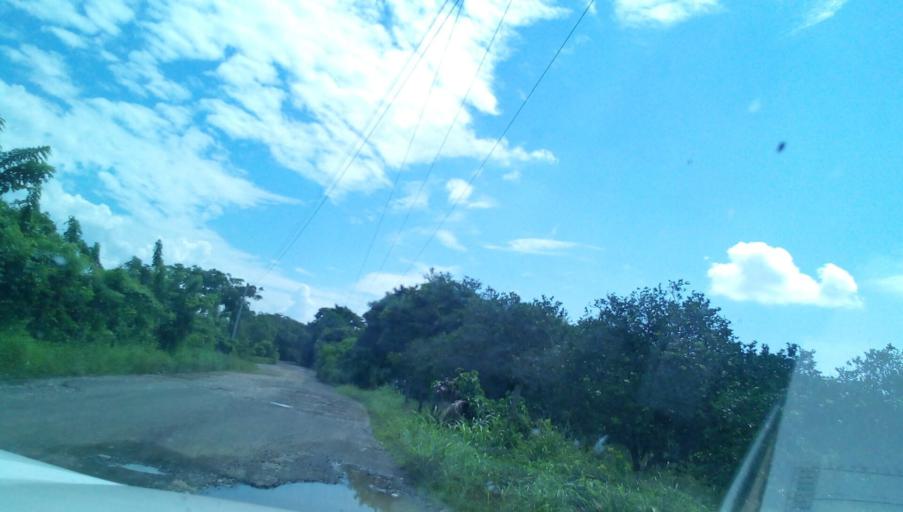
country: MX
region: Veracruz
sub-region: Alamo Temapache
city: Vegas de la Soledad y Soledad Dos
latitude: 20.9050
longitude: -97.9328
